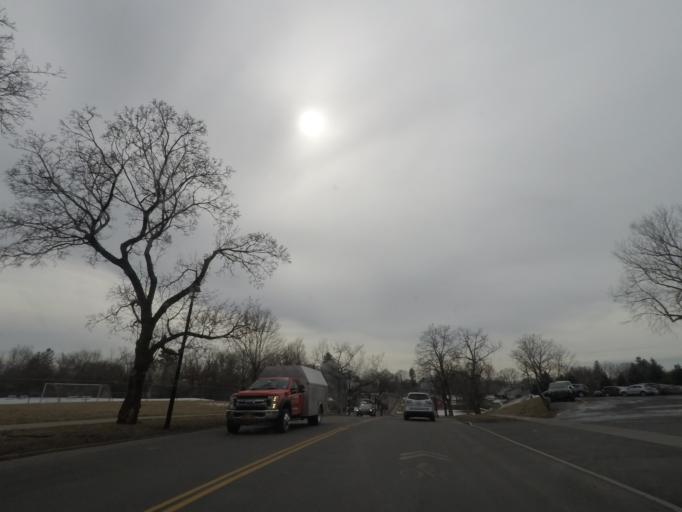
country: US
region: New York
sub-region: Albany County
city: Albany
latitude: 42.6458
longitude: -73.7858
